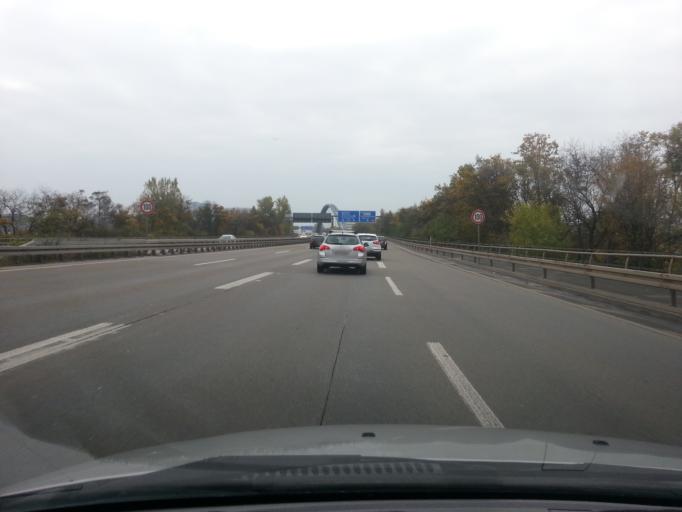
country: DE
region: Hesse
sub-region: Regierungsbezirk Darmstadt
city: Offenbach
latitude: 50.1153
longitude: 8.7328
